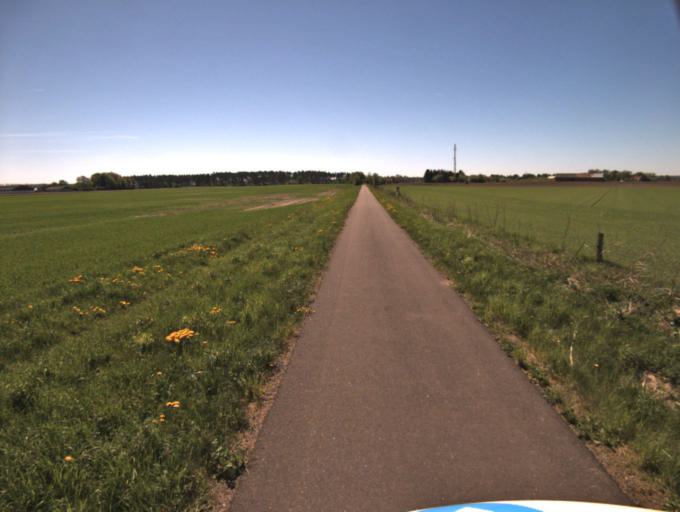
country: SE
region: Skane
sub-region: Kristianstads Kommun
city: Norra Asum
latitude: 55.9600
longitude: 14.1577
